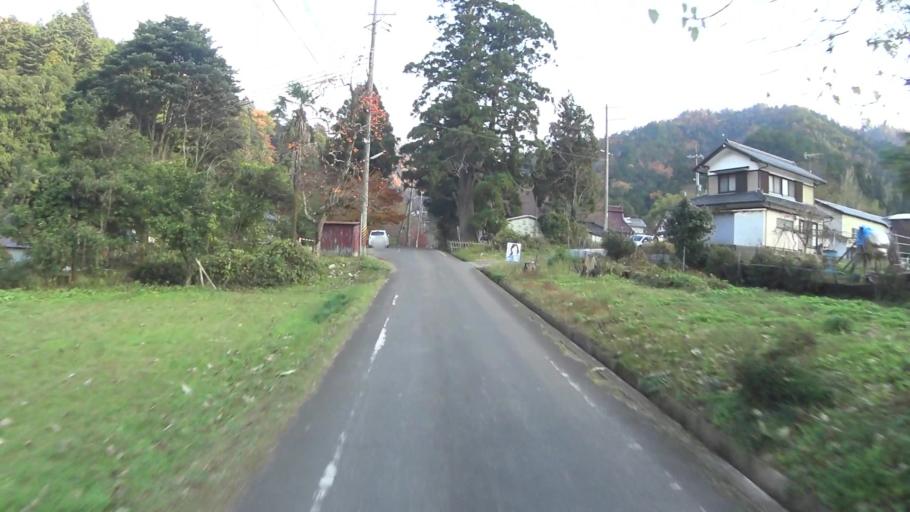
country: JP
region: Kyoto
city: Maizuru
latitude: 35.4771
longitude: 135.4451
